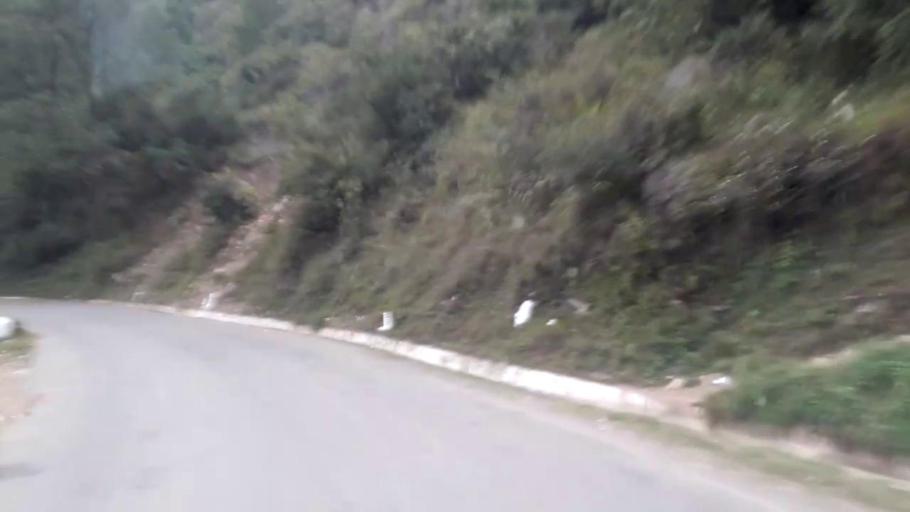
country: IN
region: Himachal Pradesh
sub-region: Shimla
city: Jutogh
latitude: 31.0492
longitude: 77.1364
